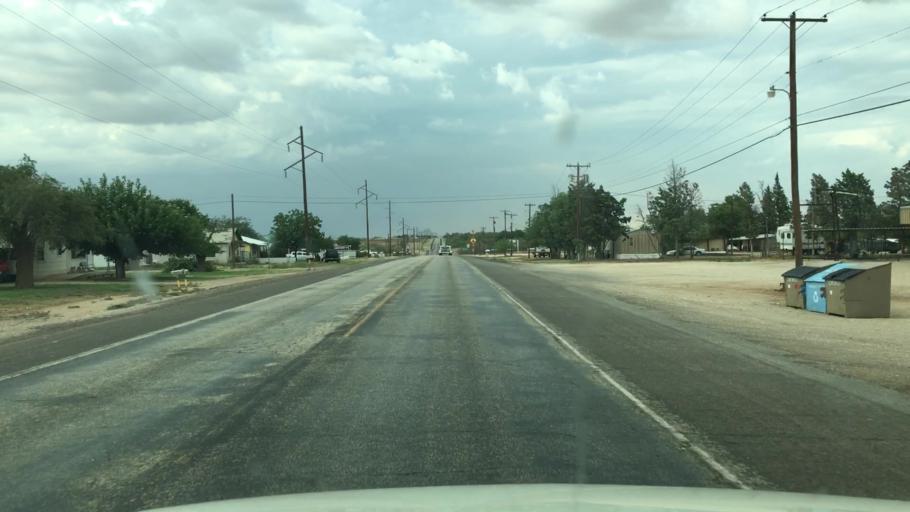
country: US
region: Texas
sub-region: Terry County
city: Brownfield
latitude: 33.1742
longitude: -102.2915
